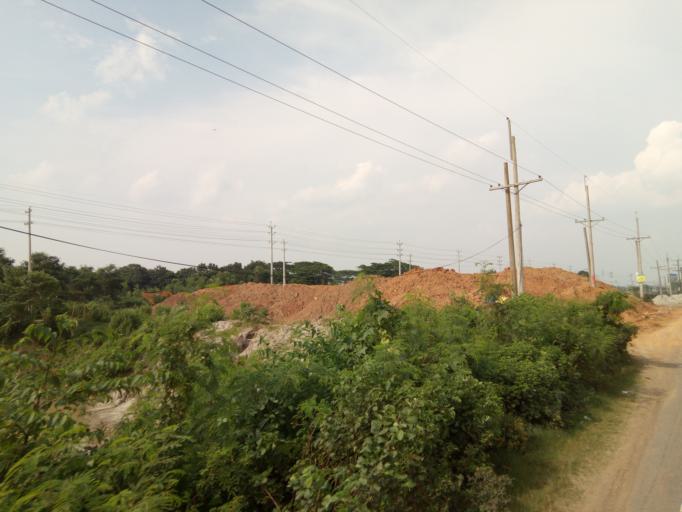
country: BD
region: Dhaka
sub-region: Dhaka
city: Dhaka
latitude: 23.6725
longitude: 90.4022
